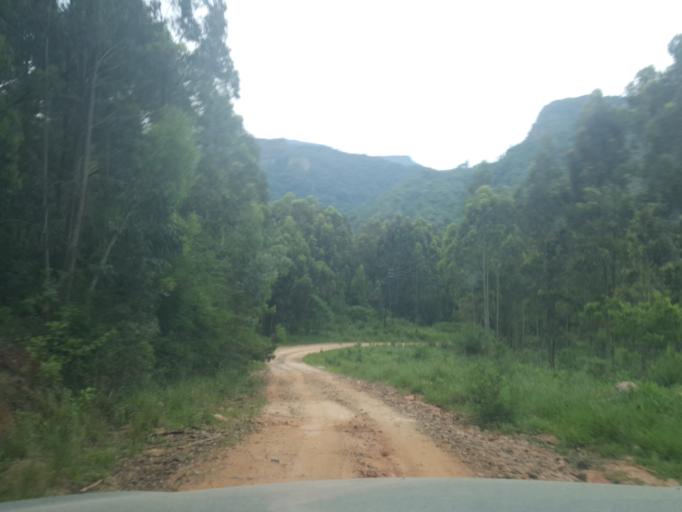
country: ZA
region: Limpopo
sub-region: Mopani District Municipality
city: Hoedspruit
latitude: -24.5931
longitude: 30.8812
